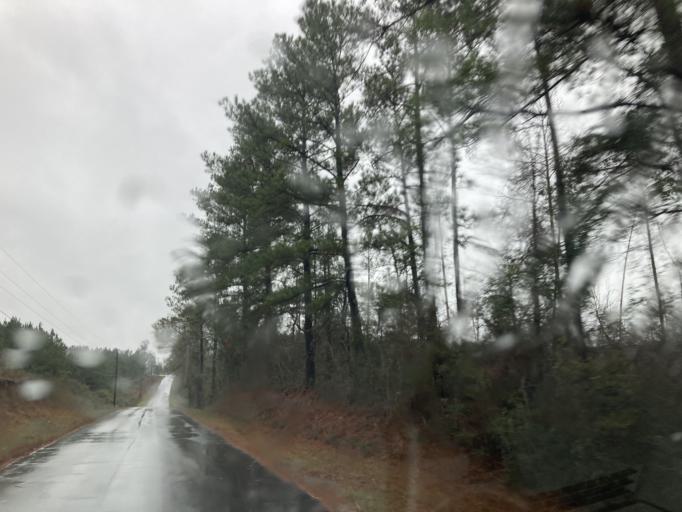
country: US
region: Mississippi
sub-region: Forrest County
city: Rawls Springs
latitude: 31.4778
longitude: -89.3823
